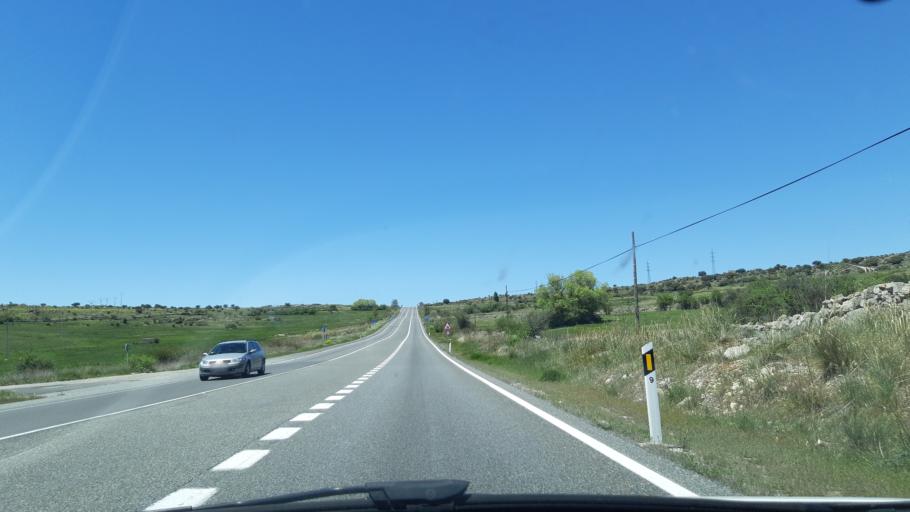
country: ES
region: Castille and Leon
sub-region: Provincia de Segovia
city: Vegas de Matute
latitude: 40.7449
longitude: -4.2778
